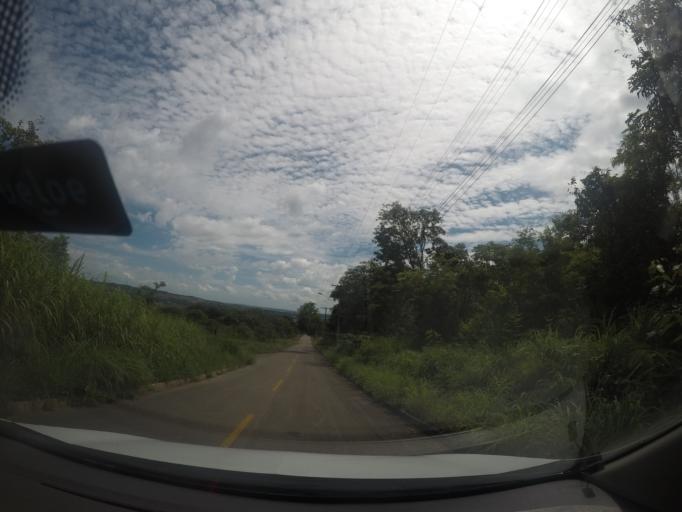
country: BR
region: Goias
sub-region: Goiania
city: Goiania
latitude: -16.6654
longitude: -49.3474
